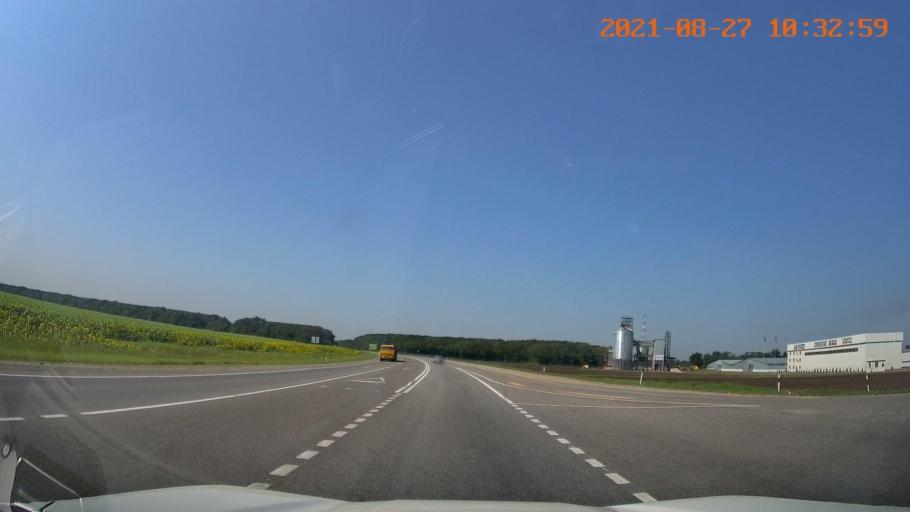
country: RU
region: Karachayevo-Cherkesiya
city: Cherkessk
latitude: 44.2624
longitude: 42.1276
